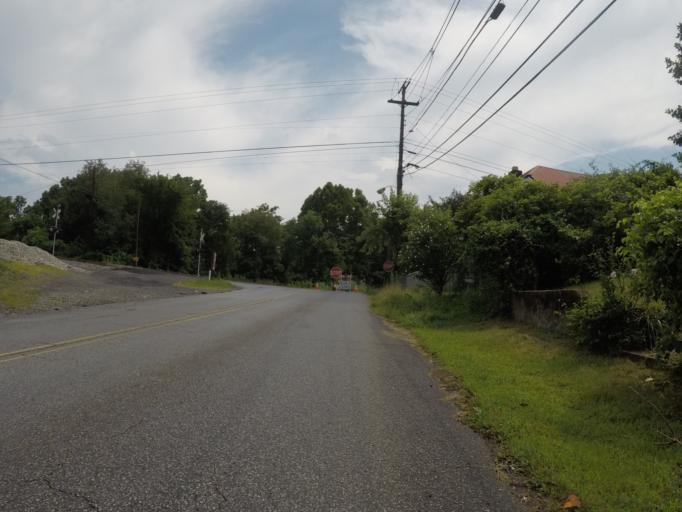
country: US
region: Kentucky
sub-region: Boyd County
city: Westwood
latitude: 38.4770
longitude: -82.6670
